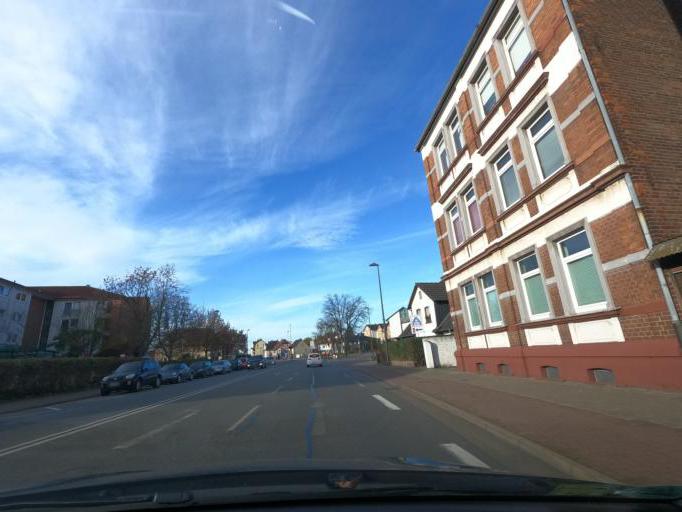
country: DE
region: Lower Saxony
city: Peine
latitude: 52.3142
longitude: 10.2337
